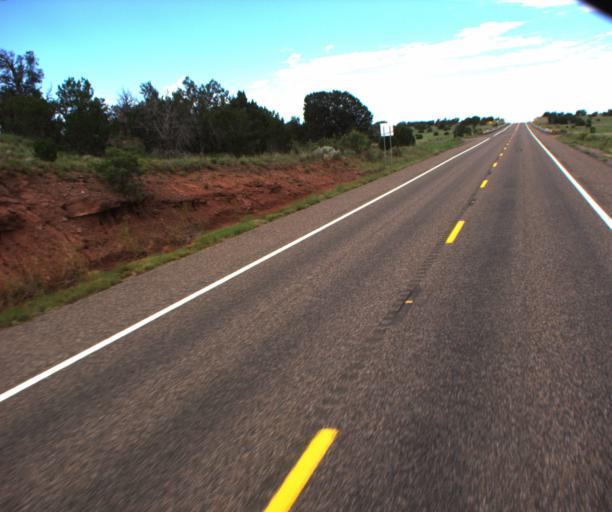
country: US
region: Arizona
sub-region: Apache County
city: Springerville
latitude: 34.1559
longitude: -109.1266
